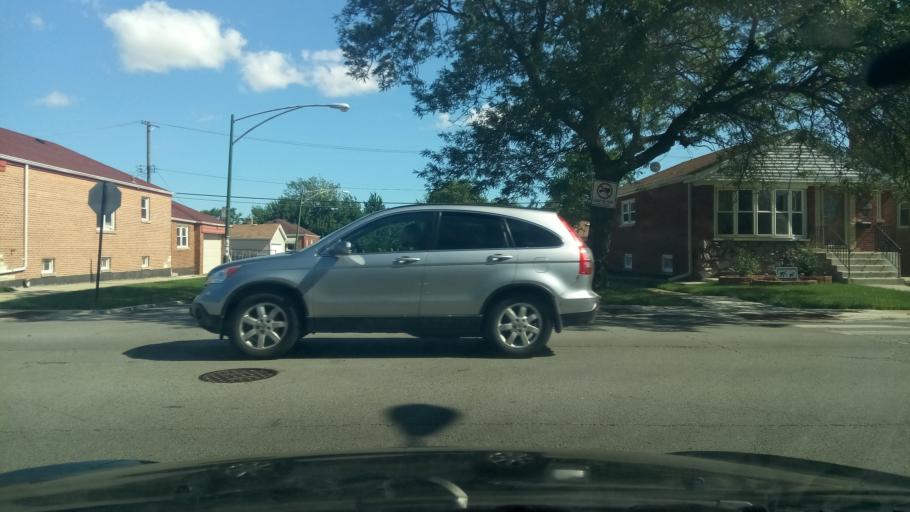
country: US
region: Illinois
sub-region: Cook County
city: Hometown
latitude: 41.7636
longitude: -87.7149
